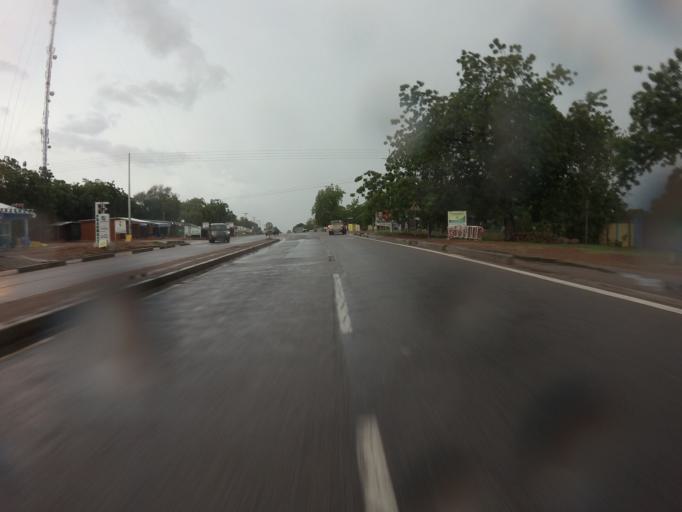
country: GH
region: Upper East
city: Bolgatanga
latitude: 10.8021
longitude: -0.8633
